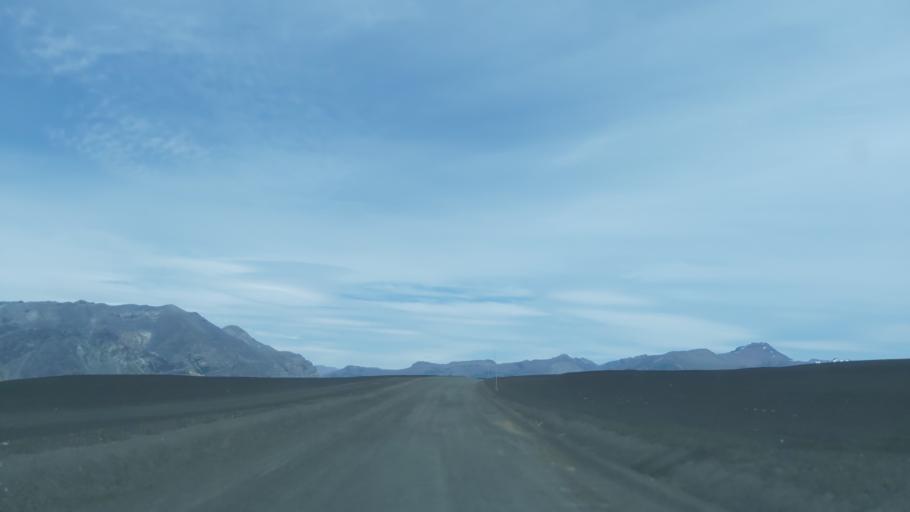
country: AR
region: Neuquen
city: Andacollo
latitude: -37.4309
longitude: -71.2859
